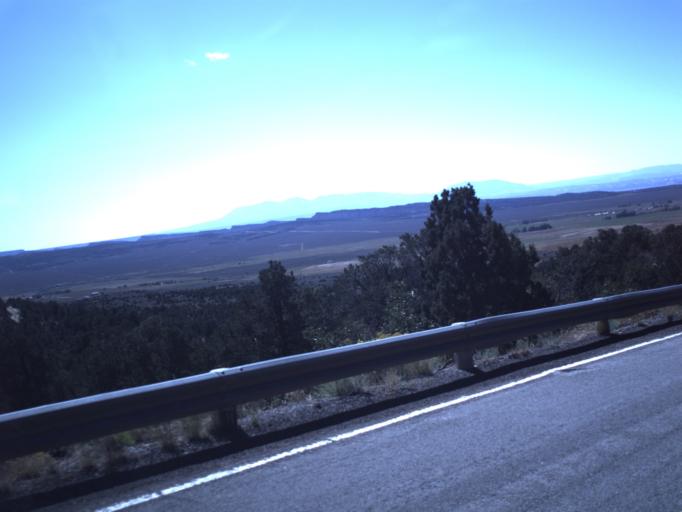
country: US
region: Utah
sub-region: Grand County
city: Moab
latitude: 38.3158
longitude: -109.2285
